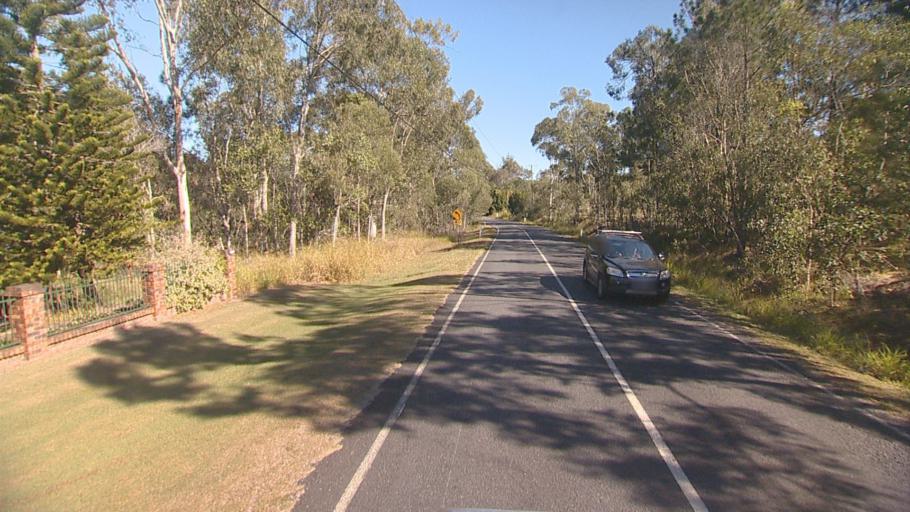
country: AU
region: Queensland
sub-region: Logan
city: Park Ridge South
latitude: -27.7216
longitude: 153.0572
